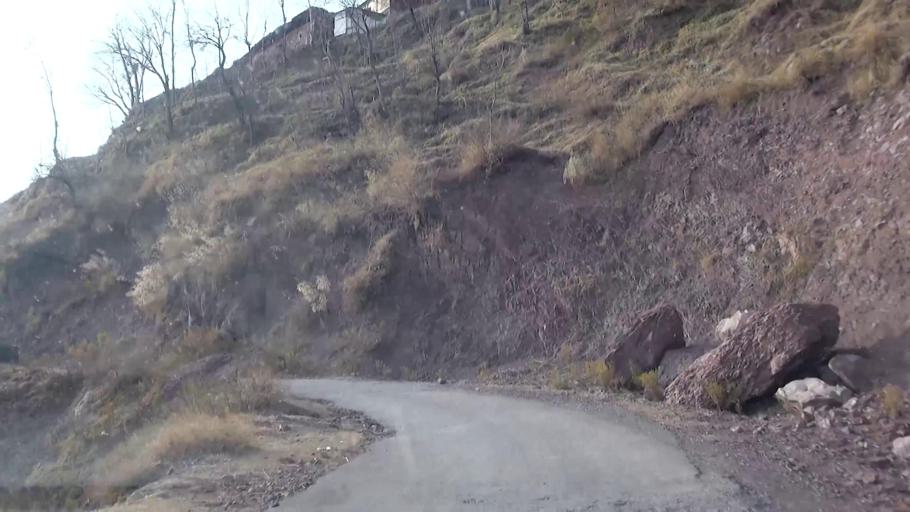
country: PK
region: Azad Kashmir
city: Muzaffarabad
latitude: 34.3697
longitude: 73.5180
